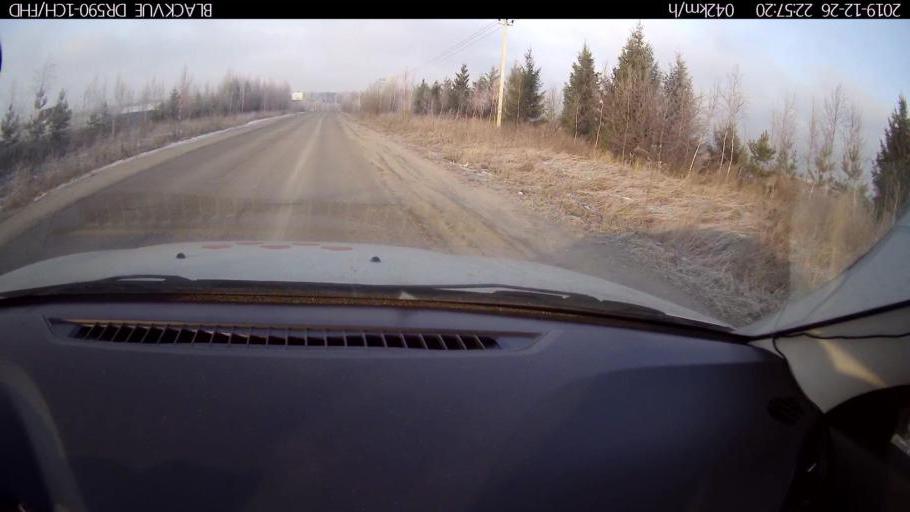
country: RU
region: Nizjnij Novgorod
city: Burevestnik
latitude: 56.1502
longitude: 43.7167
